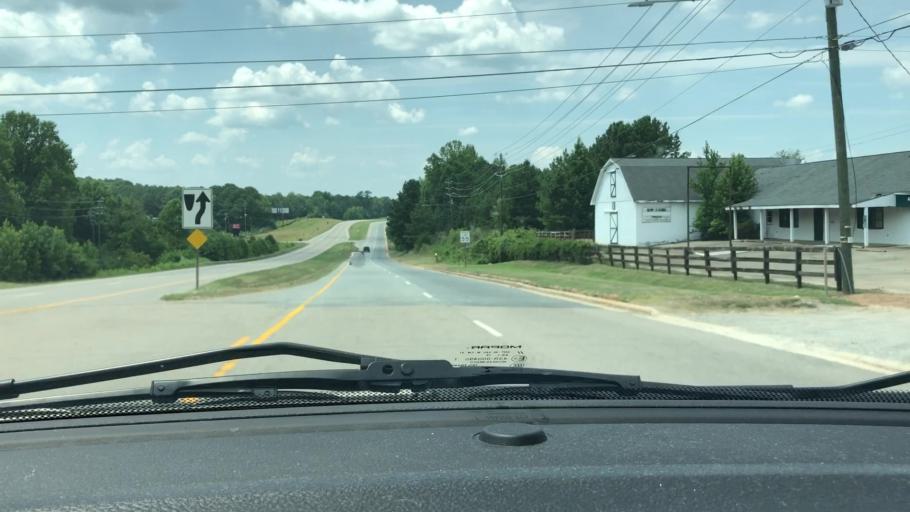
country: US
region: North Carolina
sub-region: Lee County
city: Sanford
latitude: 35.4983
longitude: -79.1997
